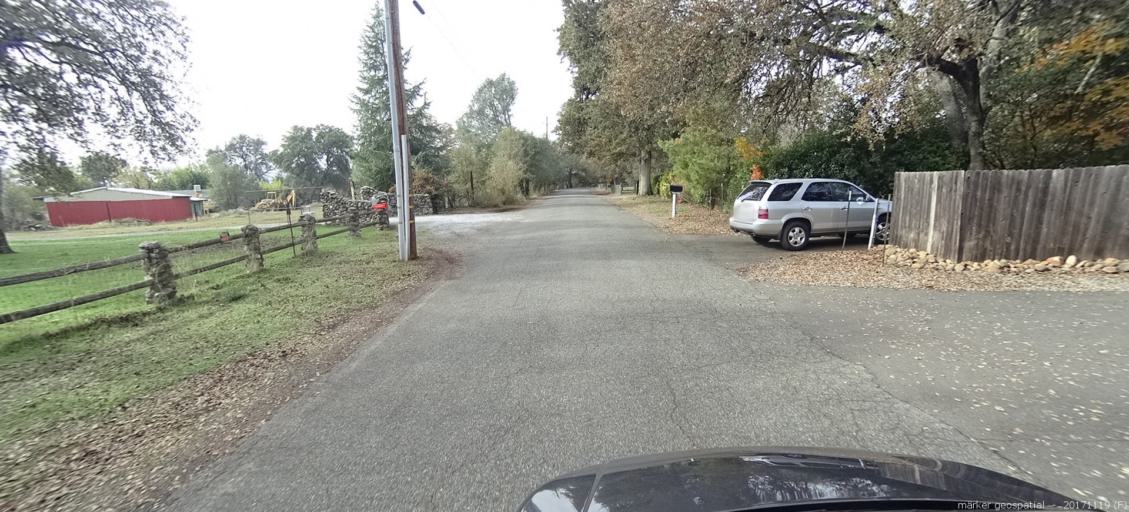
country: US
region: California
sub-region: Shasta County
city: Anderson
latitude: 40.4766
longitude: -122.2997
